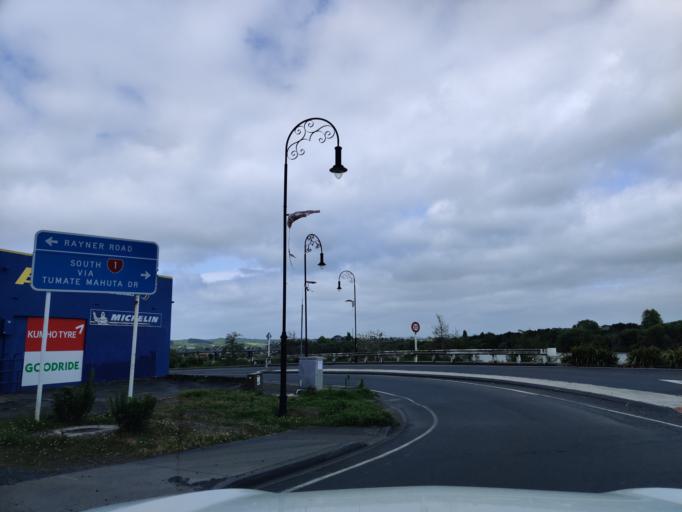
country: NZ
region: Waikato
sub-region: Waikato District
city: Ngaruawahia
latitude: -37.5615
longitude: 175.1584
